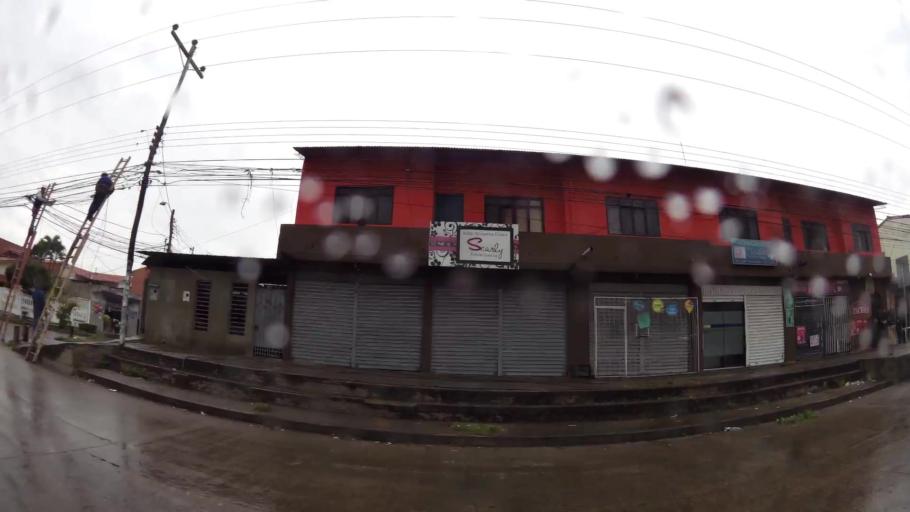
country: BO
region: Santa Cruz
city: Santa Cruz de la Sierra
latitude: -17.8001
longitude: -63.1446
